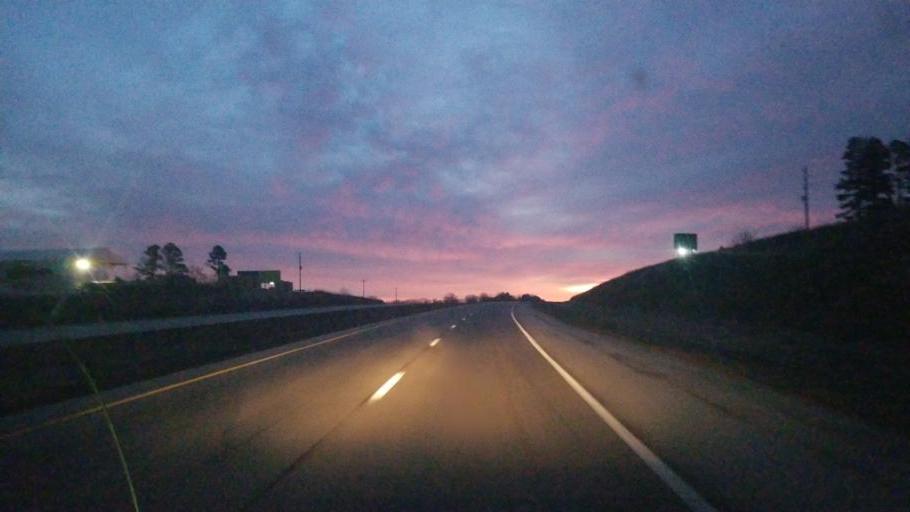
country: US
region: Missouri
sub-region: Shannon County
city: Winona
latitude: 36.9991
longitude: -91.4704
